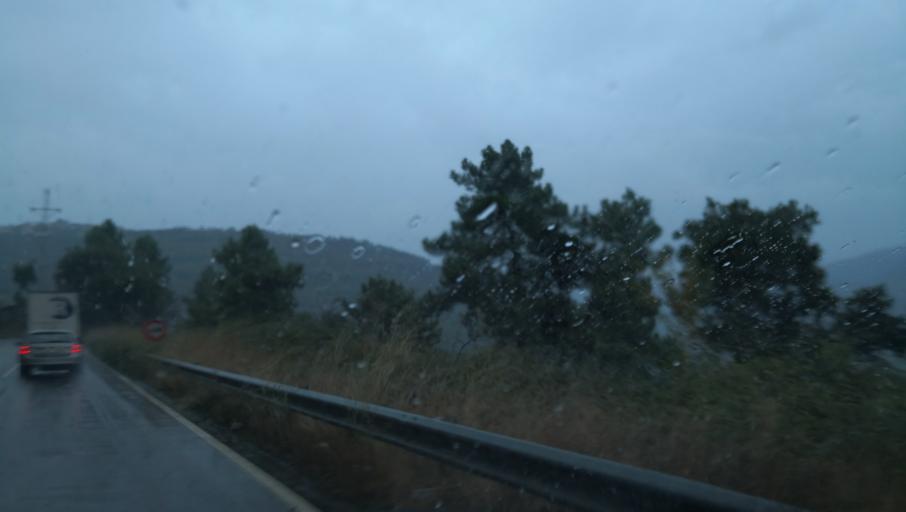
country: PT
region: Vila Real
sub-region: Santa Marta de Penaguiao
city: Santa Marta de Penaguiao
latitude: 41.2171
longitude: -7.7285
